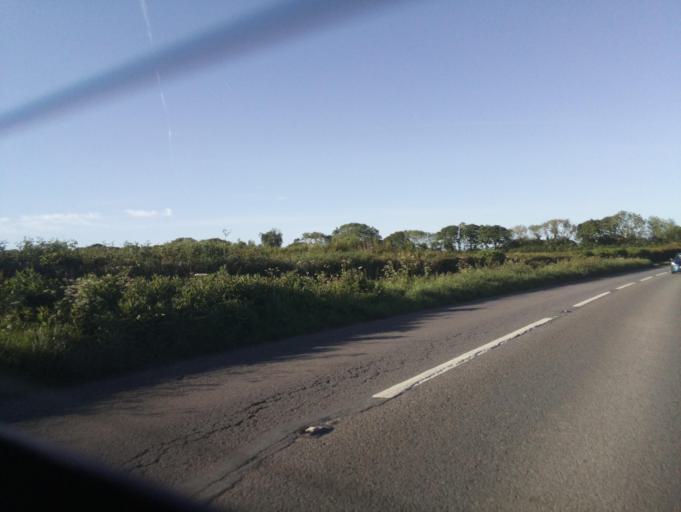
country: GB
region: England
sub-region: Devon
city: Sidmouth
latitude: 50.7126
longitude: -3.1692
